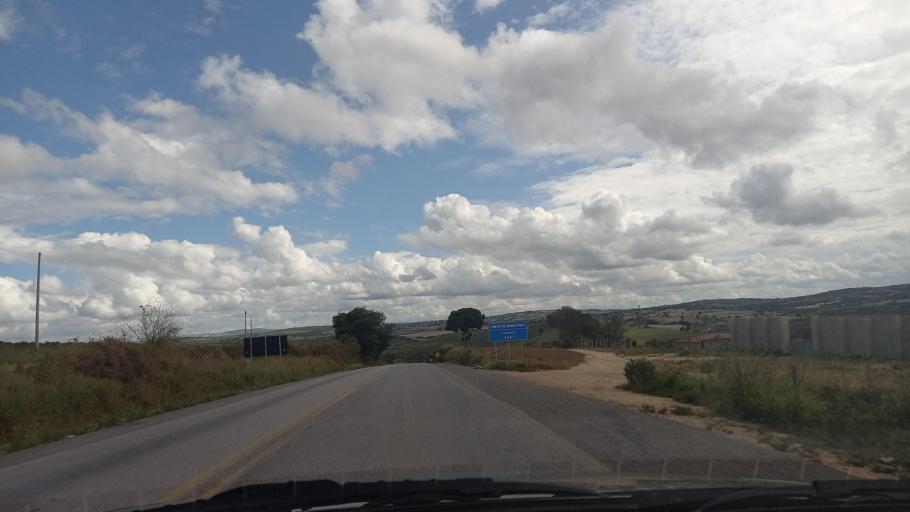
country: BR
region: Pernambuco
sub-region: Lajedo
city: Lajedo
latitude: -8.7235
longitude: -36.4281
